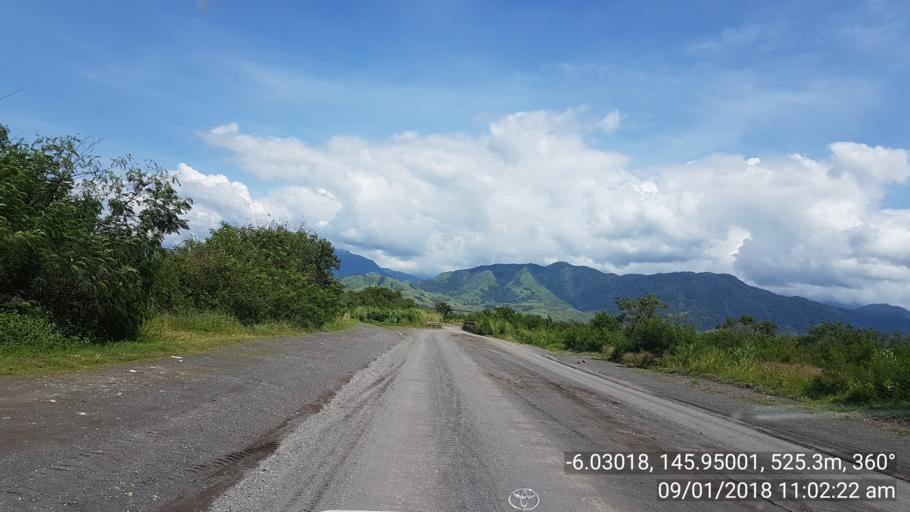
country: PG
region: Eastern Highlands
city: Kainantu
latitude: -6.0304
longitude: 145.9501
